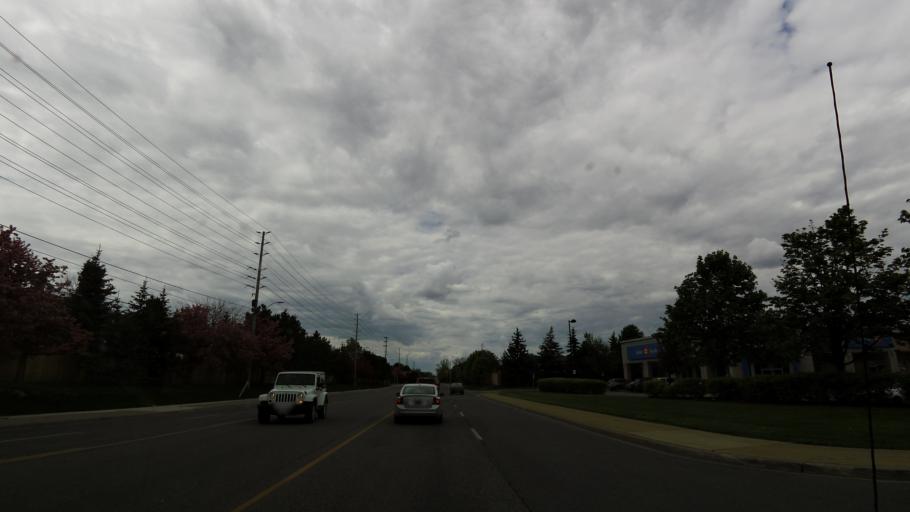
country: CA
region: Ontario
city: Mississauga
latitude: 43.5986
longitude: -79.7133
